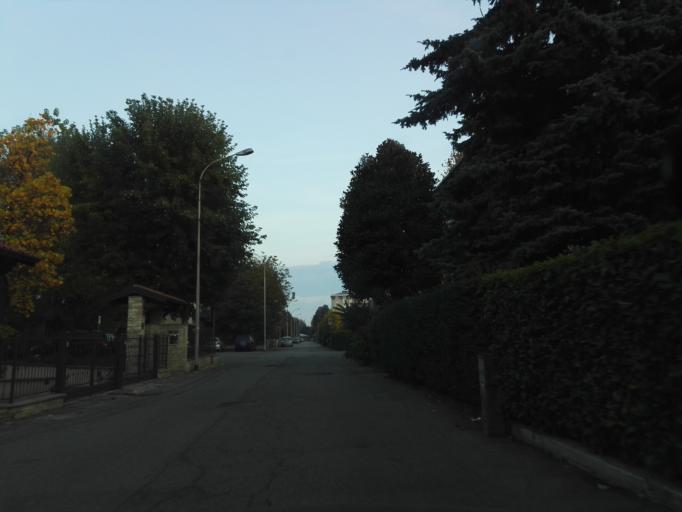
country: IT
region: Lombardy
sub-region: Citta metropolitana di Milano
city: San Giuliano Milanese
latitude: 45.4044
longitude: 9.2888
